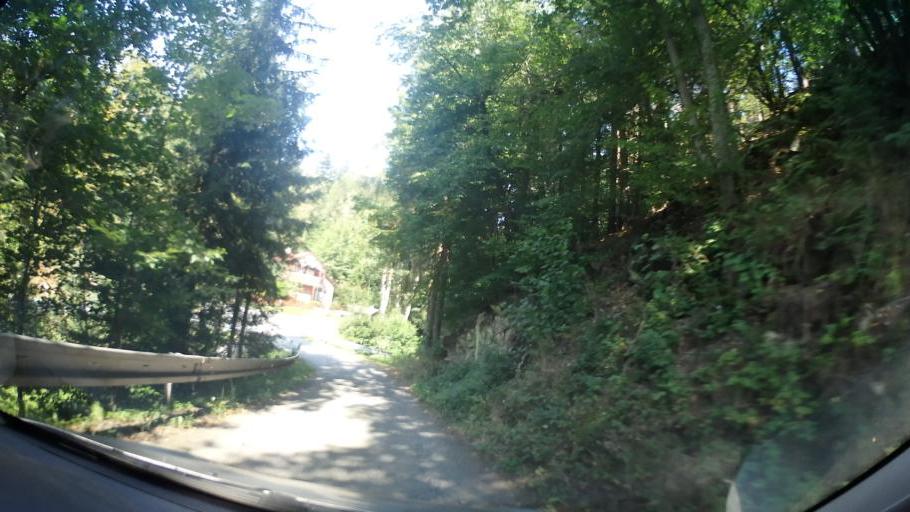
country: CZ
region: Pardubicky
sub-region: Okres Svitavy
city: Bystre
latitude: 49.5684
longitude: 16.3447
